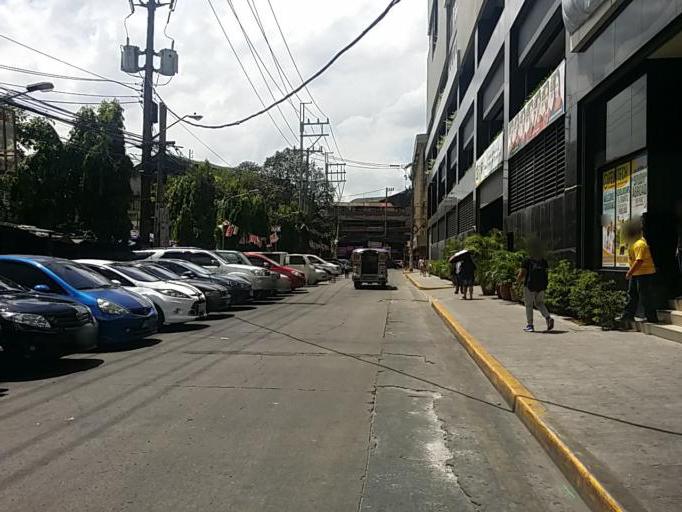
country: PH
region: Metro Manila
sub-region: City of Manila
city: Manila
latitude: 14.6045
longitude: 120.9885
